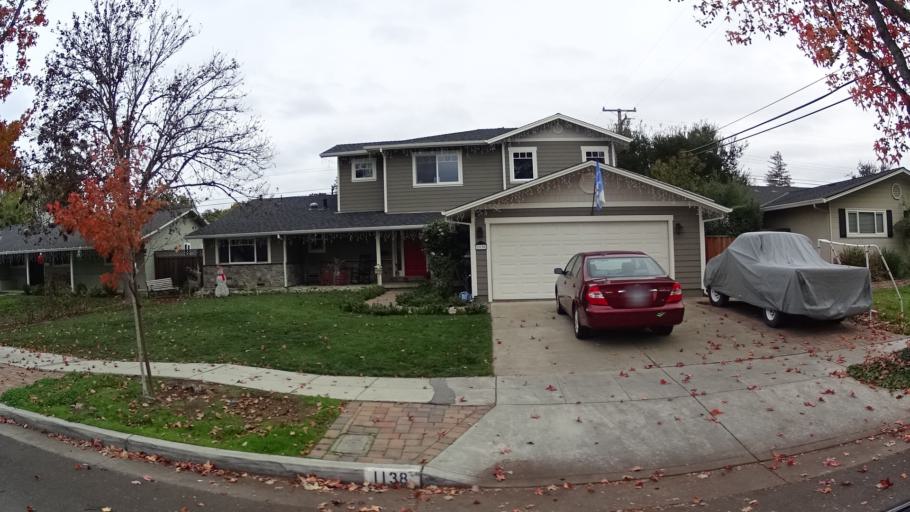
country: US
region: California
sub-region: Santa Clara County
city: Sunnyvale
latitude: 37.3574
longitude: -122.0473
